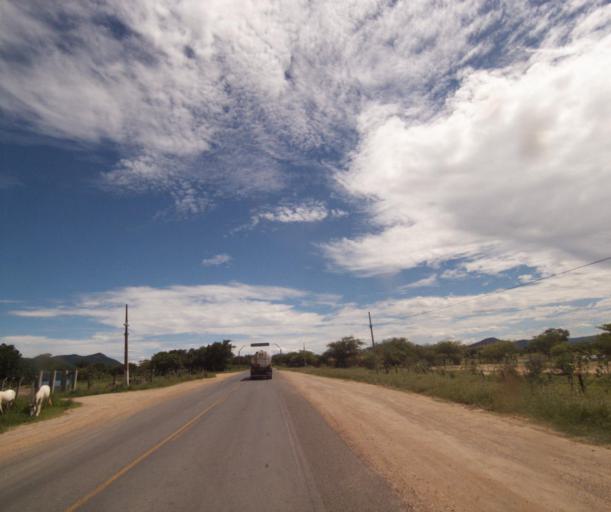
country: BR
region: Bahia
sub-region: Guanambi
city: Guanambi
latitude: -14.2490
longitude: -42.7818
